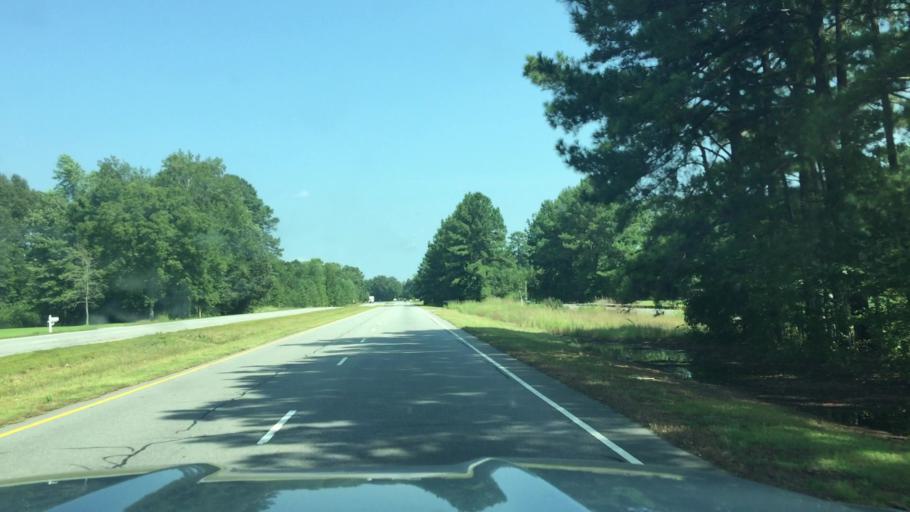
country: US
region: North Carolina
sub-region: Martin County
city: Williamston
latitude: 35.8077
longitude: -76.9504
